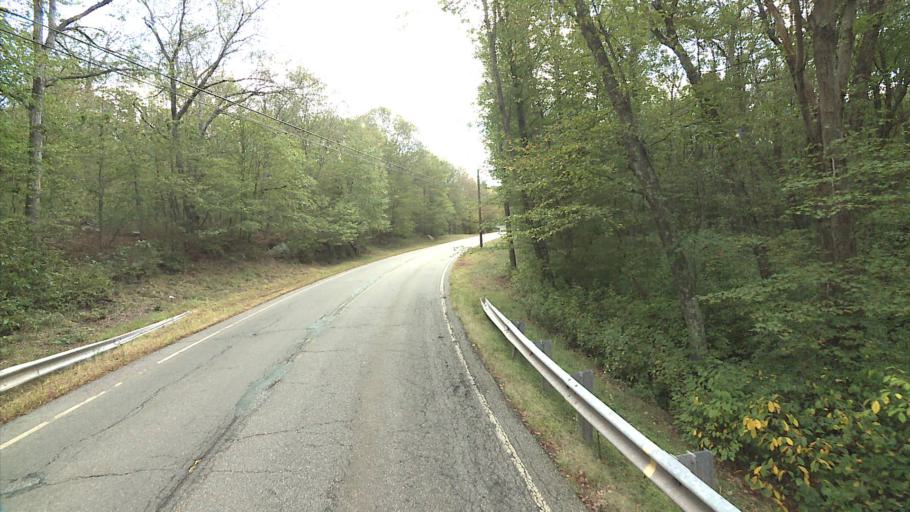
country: US
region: Connecticut
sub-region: Middlesex County
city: Durham
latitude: 41.4321
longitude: -72.6398
